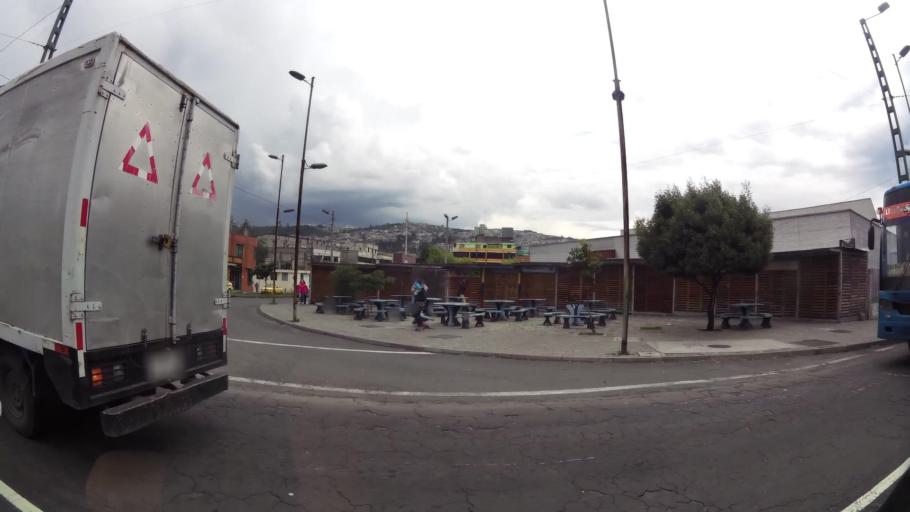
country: EC
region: Pichincha
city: Quito
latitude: -0.2771
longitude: -78.5424
